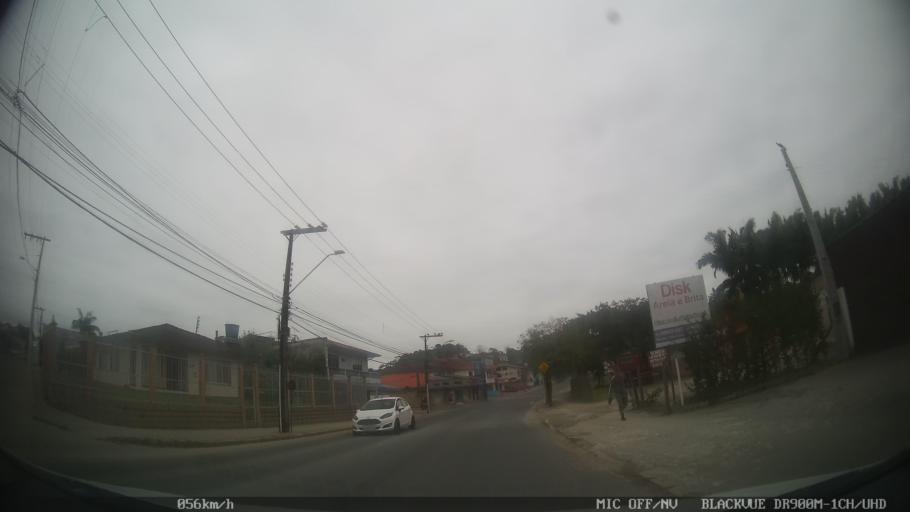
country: BR
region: Santa Catarina
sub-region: Joinville
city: Joinville
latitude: -26.3340
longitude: -48.8341
